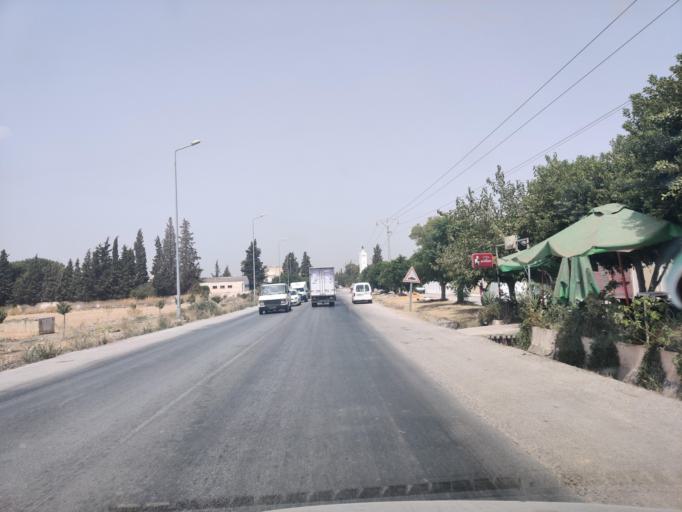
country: TN
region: Tunis
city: La Sebala du Mornag
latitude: 36.6606
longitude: 10.3267
